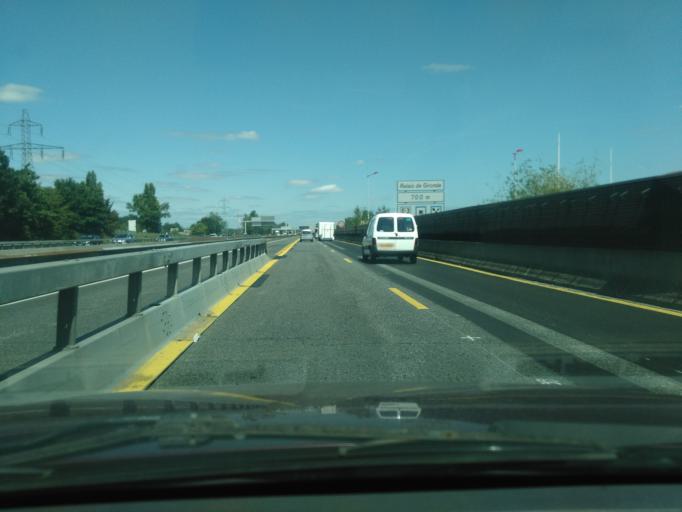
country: FR
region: Aquitaine
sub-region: Departement de la Gironde
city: Le Haillan
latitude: 44.8436
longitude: -0.6723
